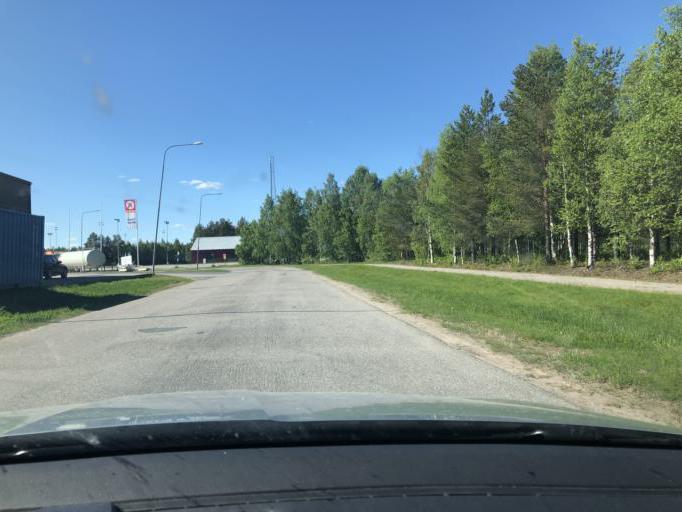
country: SE
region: Norrbotten
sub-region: Kalix Kommun
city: Kalix
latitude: 65.8529
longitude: 23.1858
